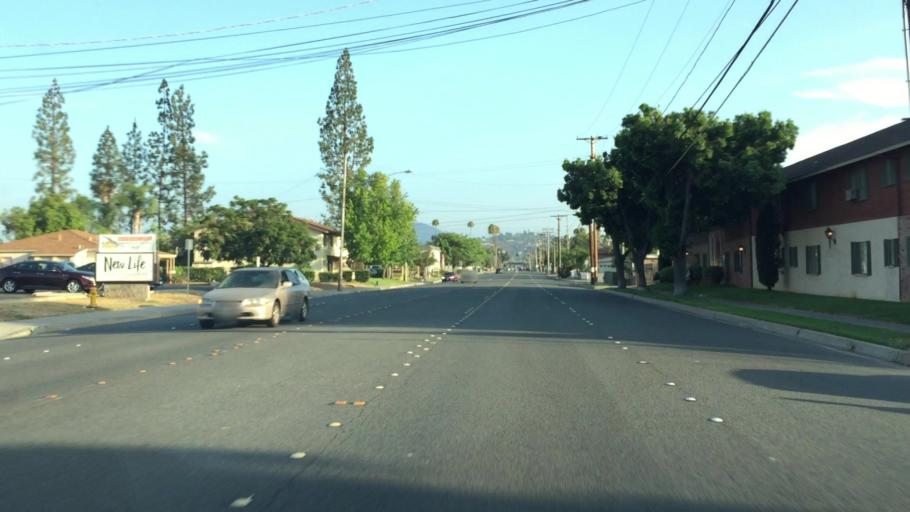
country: US
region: California
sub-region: San Diego County
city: Bostonia
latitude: 32.8106
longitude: -116.9510
